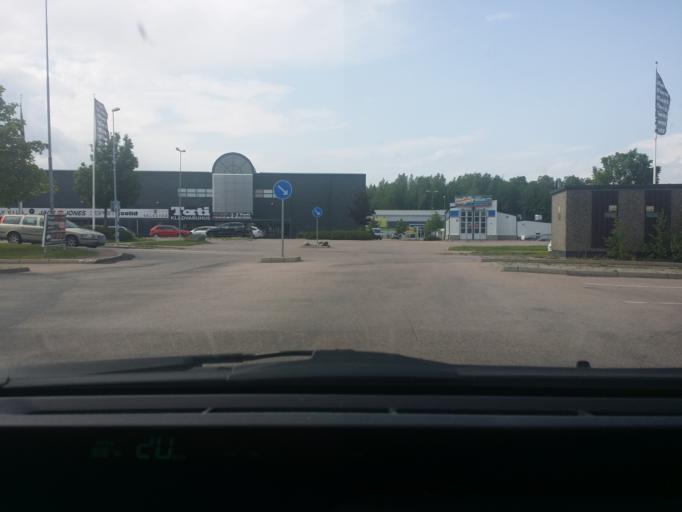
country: SE
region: Vaestmanland
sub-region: Vasteras
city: Vasteras
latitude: 59.6105
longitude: 16.4644
